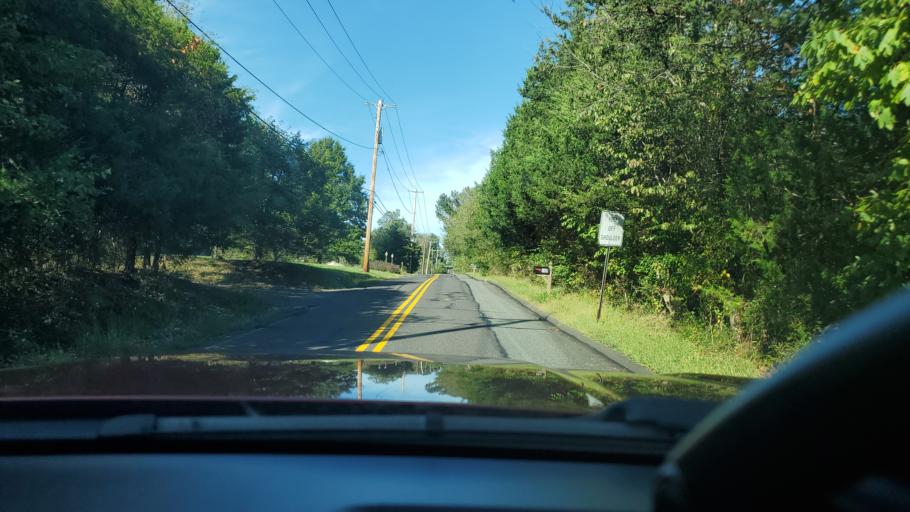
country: US
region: Pennsylvania
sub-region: Montgomery County
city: Spring Mount
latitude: 40.3065
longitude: -75.5195
